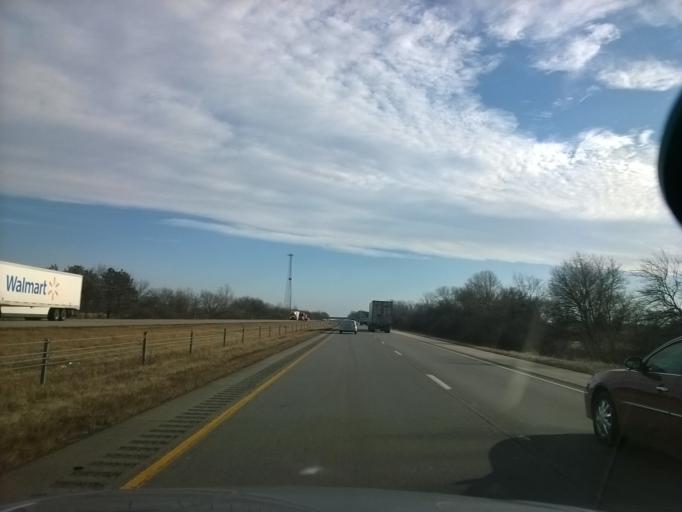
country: US
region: Indiana
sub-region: Johnson County
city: Franklin
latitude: 39.4614
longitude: -86.0029
